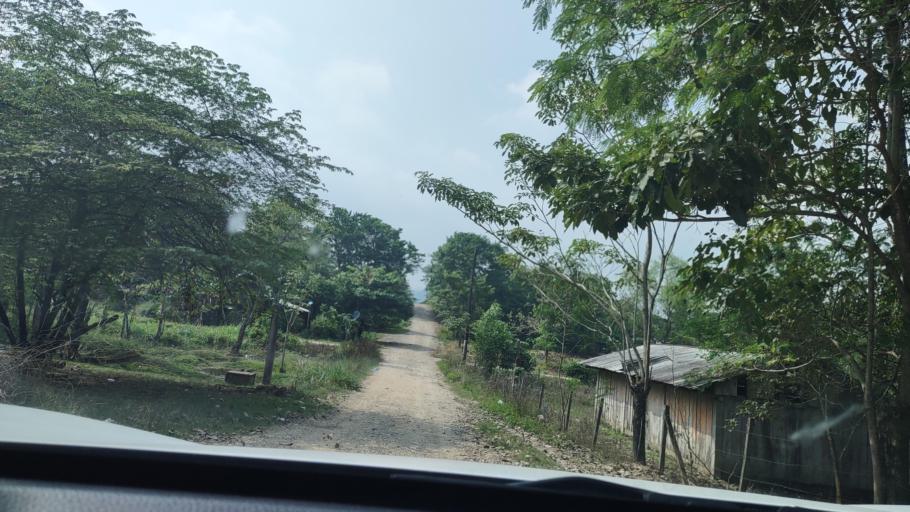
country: MX
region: Veracruz
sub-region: Uxpanapa
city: Poblado 10
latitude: 17.5462
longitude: -94.2902
